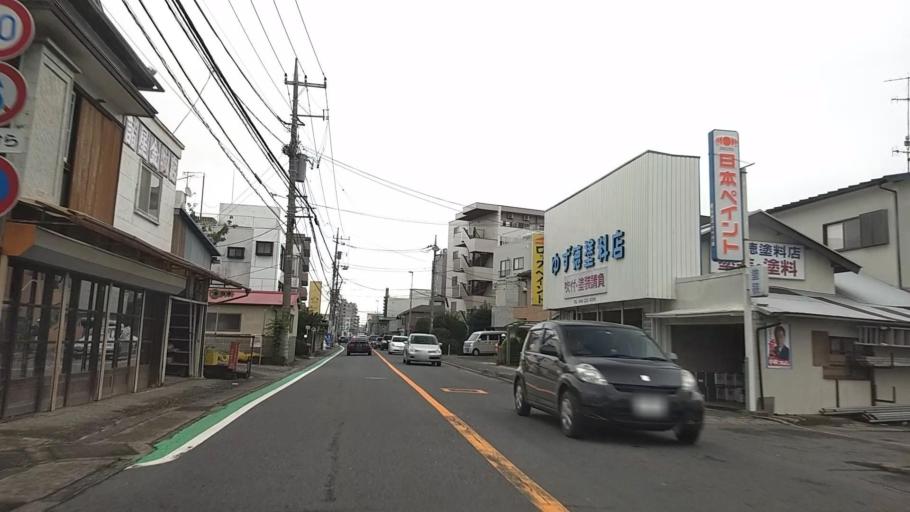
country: JP
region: Kanagawa
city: Atsugi
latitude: 35.4486
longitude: 139.3617
